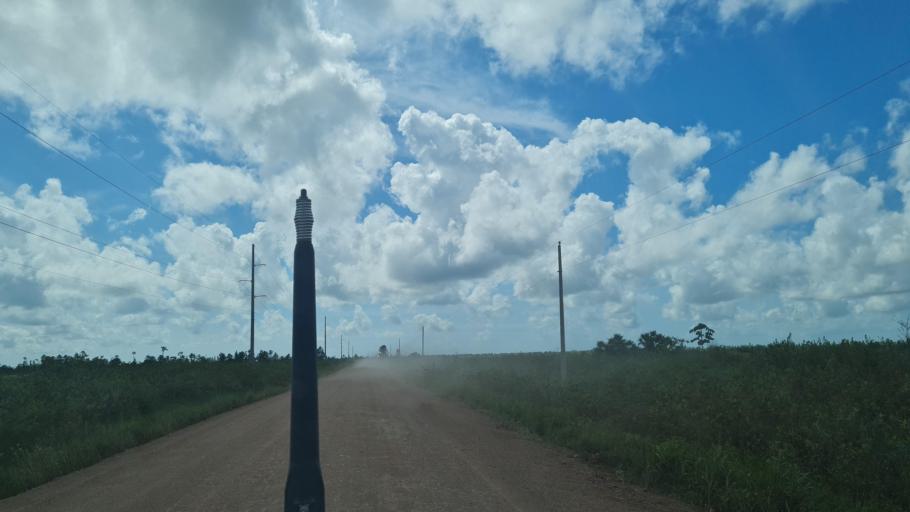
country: NI
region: Atlantico Norte (RAAN)
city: Puerto Cabezas
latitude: 14.1089
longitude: -83.5791
